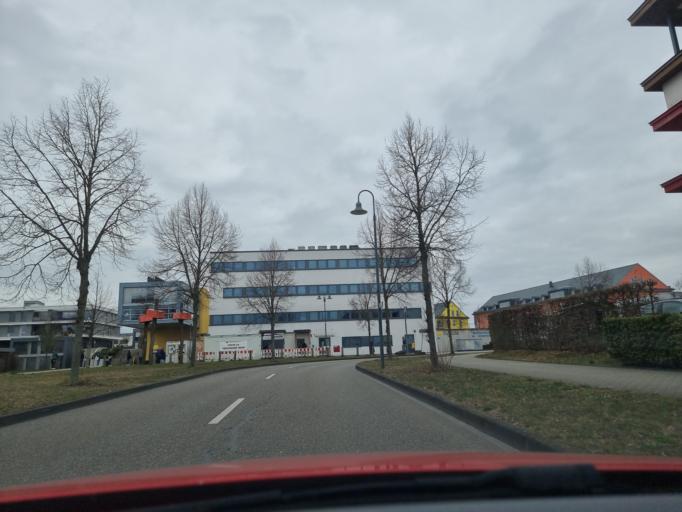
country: DE
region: Rheinland-Pfalz
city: Trier
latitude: 49.7554
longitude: 6.6719
